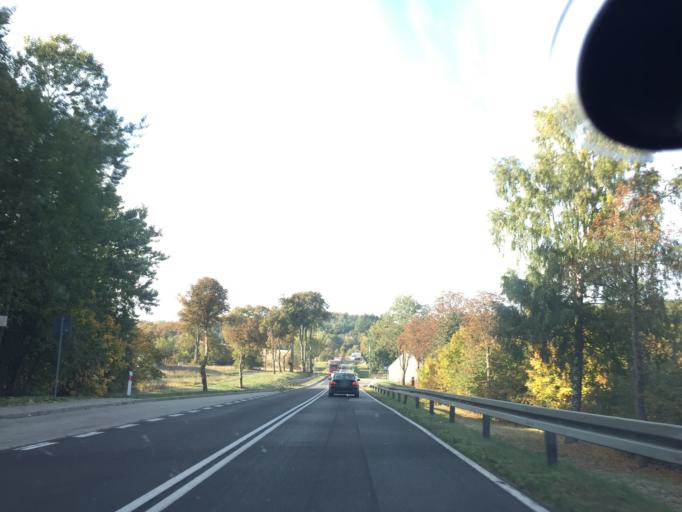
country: PL
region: Warmian-Masurian Voivodeship
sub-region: Powiat lidzbarski
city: Lidzbark Warminski
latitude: 54.0741
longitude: 20.5029
